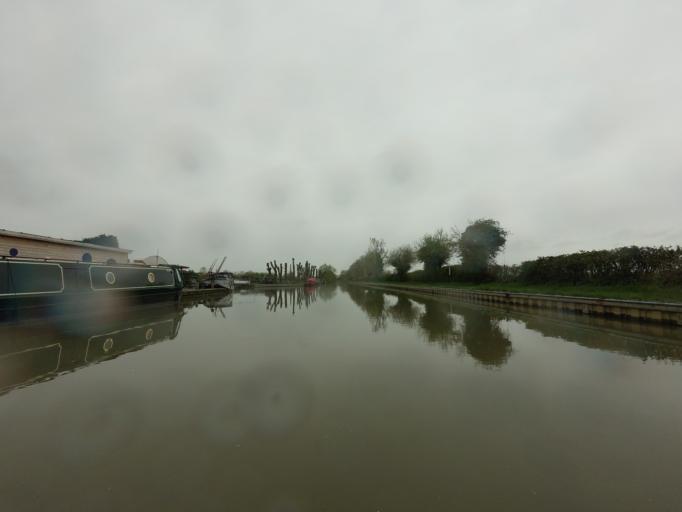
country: GB
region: England
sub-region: Milton Keynes
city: Castlethorpe
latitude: 52.1010
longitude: -0.8816
